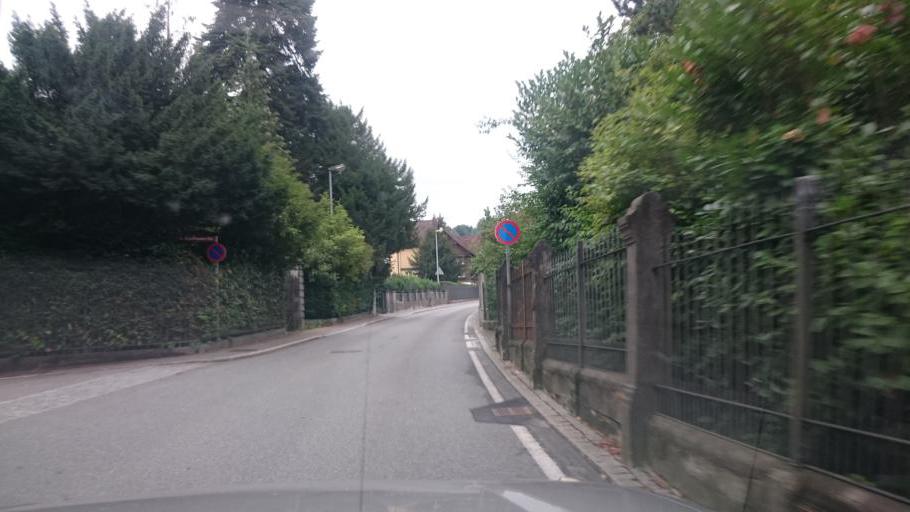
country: AT
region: Vorarlberg
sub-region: Politischer Bezirk Dornbirn
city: Dornbirn
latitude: 47.4118
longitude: 9.7473
